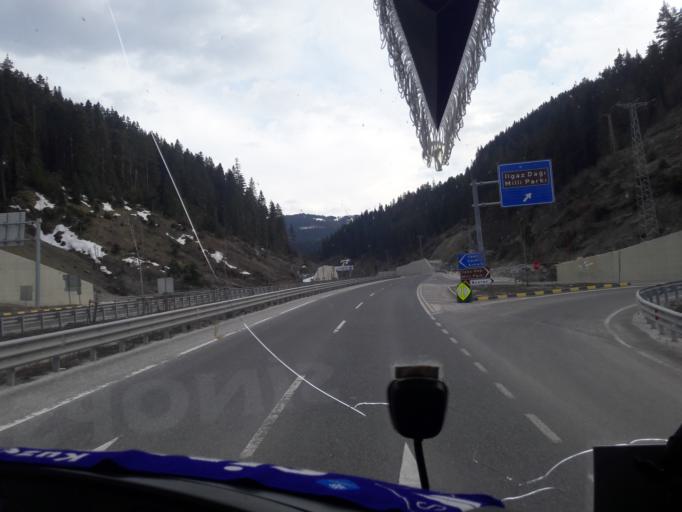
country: TR
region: Kastamonu
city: Kuzyaka
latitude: 41.0995
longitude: 33.7510
